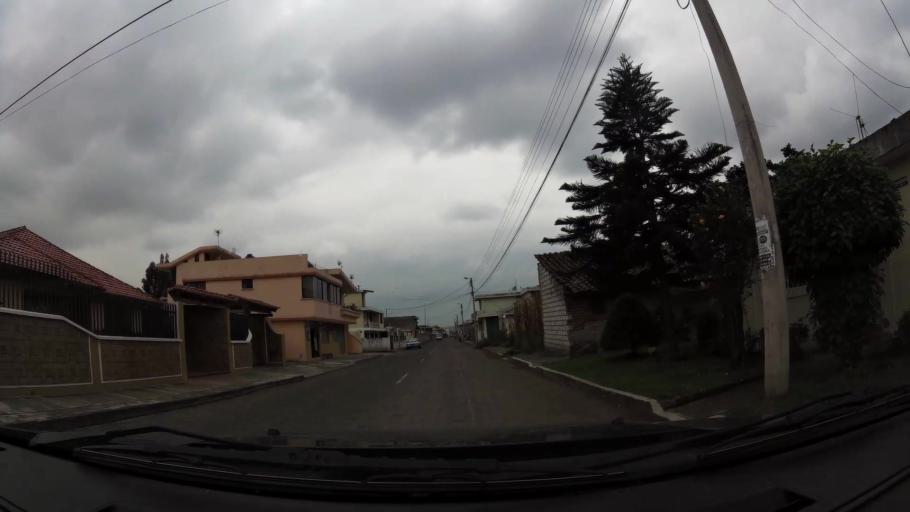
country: EC
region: Pichincha
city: Sangolqui
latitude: -0.3394
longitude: -78.4727
